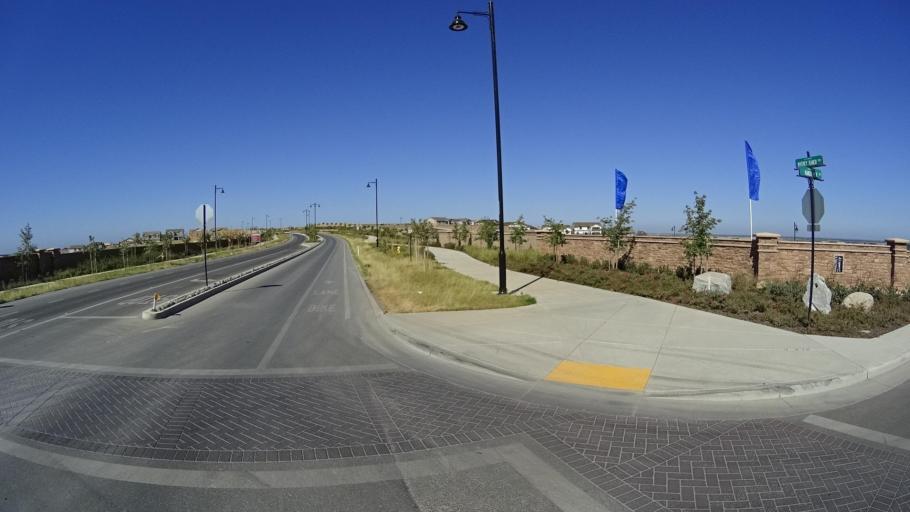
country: US
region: California
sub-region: Placer County
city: Rocklin
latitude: 38.8371
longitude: -121.2602
